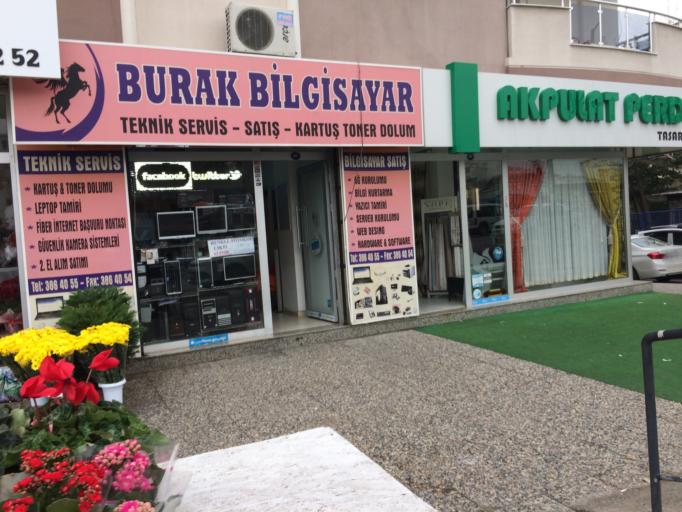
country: TR
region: Izmir
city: Karsiyaka
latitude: 38.4925
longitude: 27.0612
